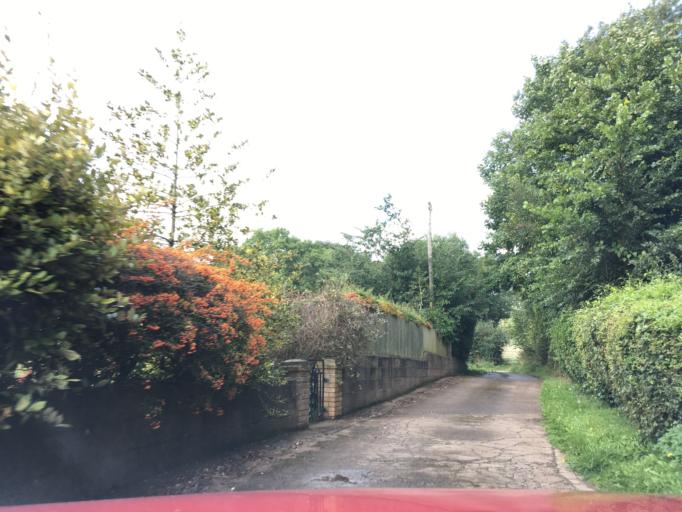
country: GB
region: England
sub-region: South Gloucestershire
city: Tytherington
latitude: 51.5912
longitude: -2.4865
